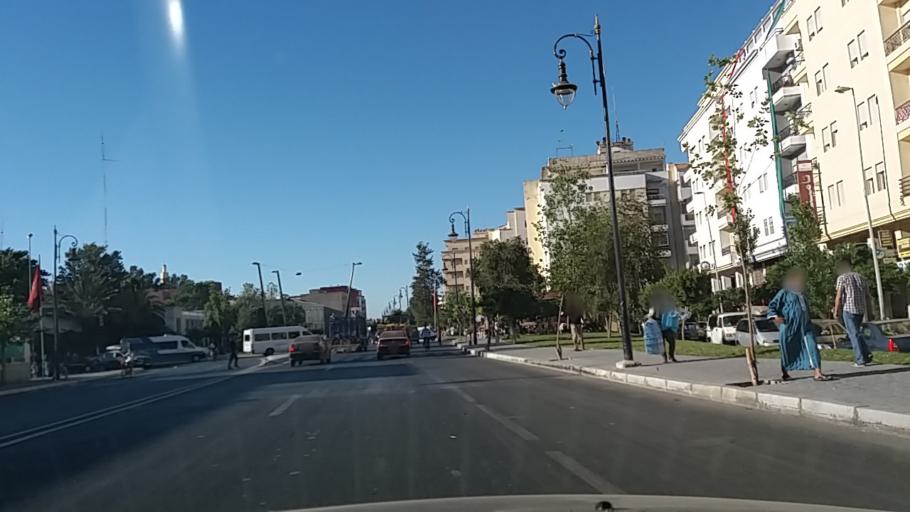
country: MA
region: Tanger-Tetouan
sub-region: Tanger-Assilah
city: Tangier
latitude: 35.7427
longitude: -5.7992
